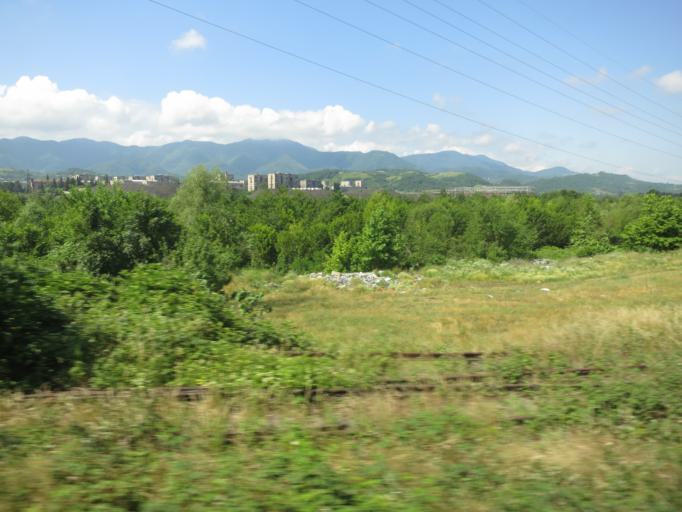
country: GE
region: Imereti
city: Zestap'oni
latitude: 42.1155
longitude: 43.0198
